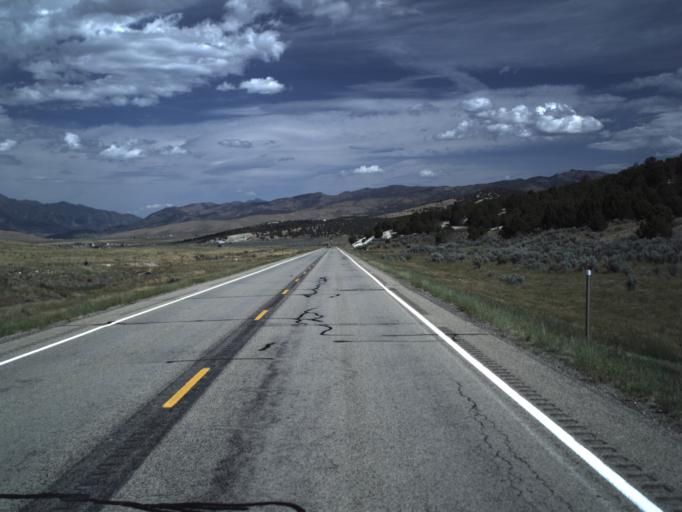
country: US
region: Utah
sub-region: Sanpete County
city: Fairview
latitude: 39.7381
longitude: -111.4771
